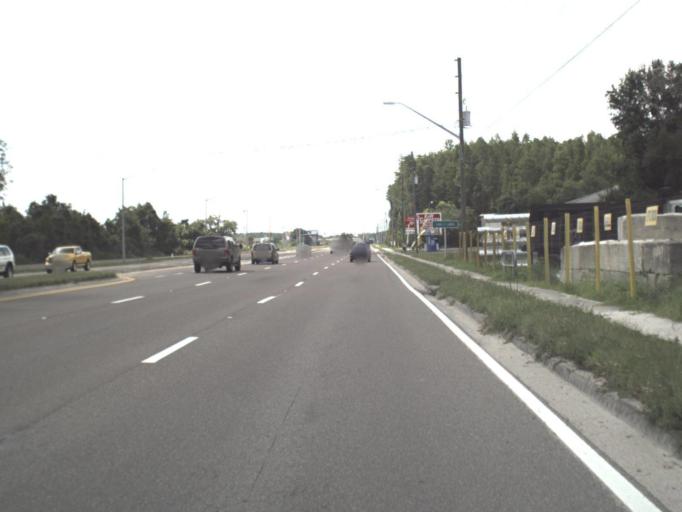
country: US
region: Florida
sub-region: Hillsborough County
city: Lutz
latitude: 28.1737
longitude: -82.4621
